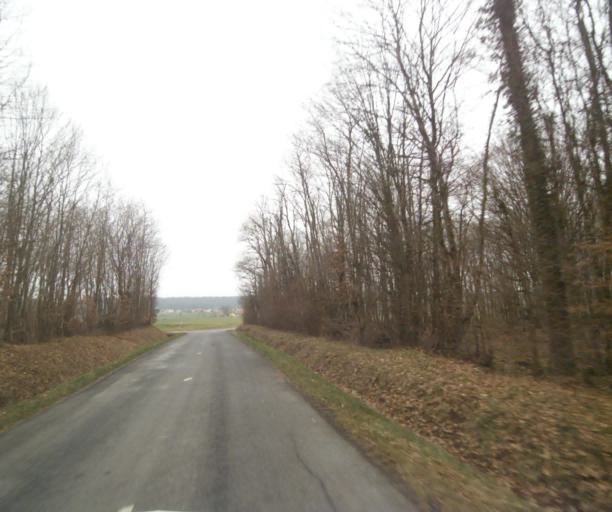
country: FR
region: Champagne-Ardenne
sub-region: Departement de la Haute-Marne
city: Bienville
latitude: 48.5469
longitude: 4.9897
